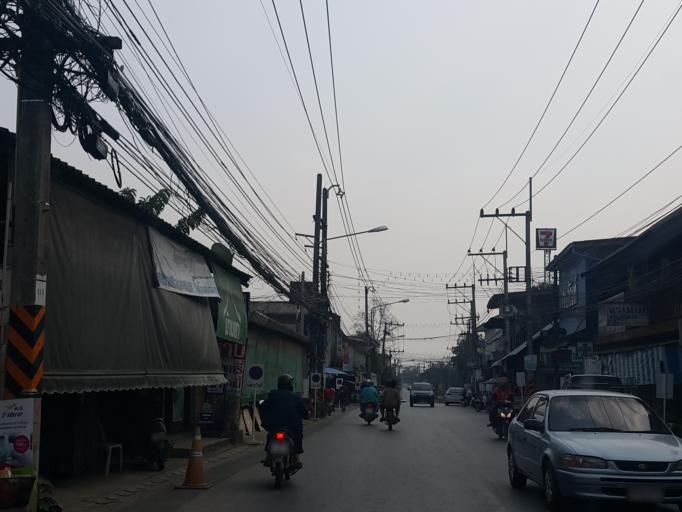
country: TH
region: Chiang Mai
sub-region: Amphoe Chiang Dao
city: Chiang Dao
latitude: 19.3685
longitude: 98.9650
